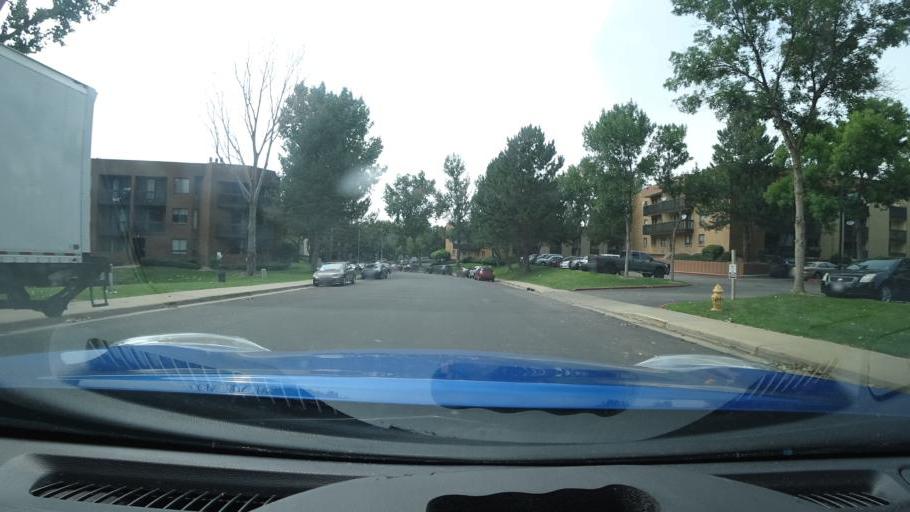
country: US
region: Colorado
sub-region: Arapahoe County
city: Glendale
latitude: 39.6697
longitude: -104.8722
